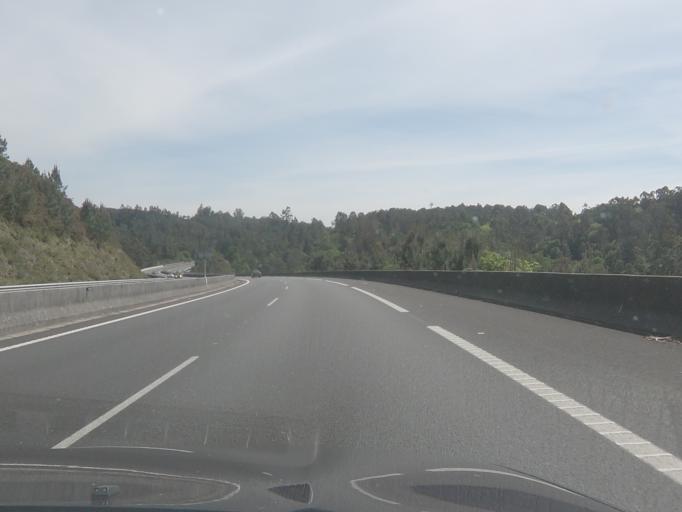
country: ES
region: Galicia
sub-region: Provincia de Pontevedra
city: Valga
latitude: 42.6807
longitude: -8.6347
